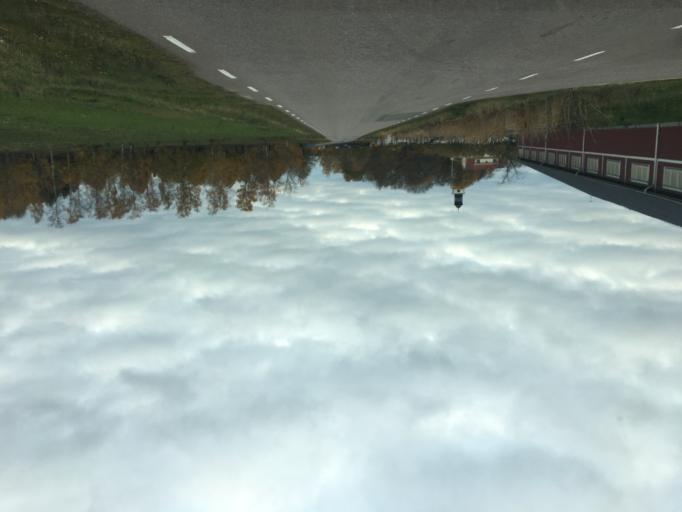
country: SE
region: Soedermanland
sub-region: Eskilstuna Kommun
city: Kvicksund
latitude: 59.5670
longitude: 16.4061
